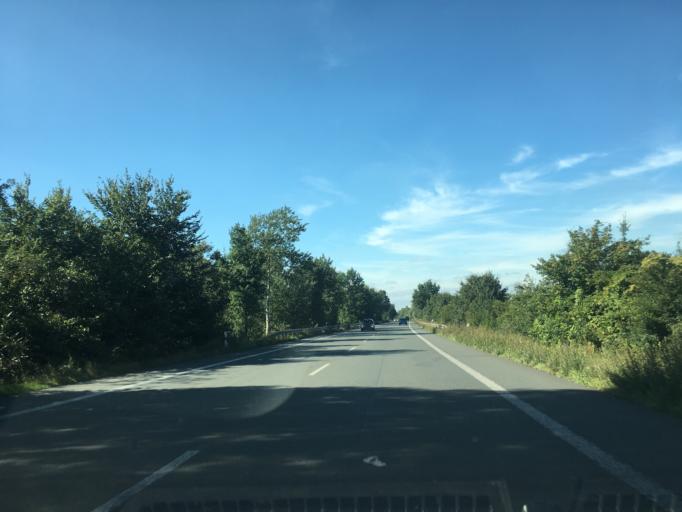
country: DE
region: North Rhine-Westphalia
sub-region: Regierungsbezirk Detmold
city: Rheda-Wiedenbruck
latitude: 51.8715
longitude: 8.3042
